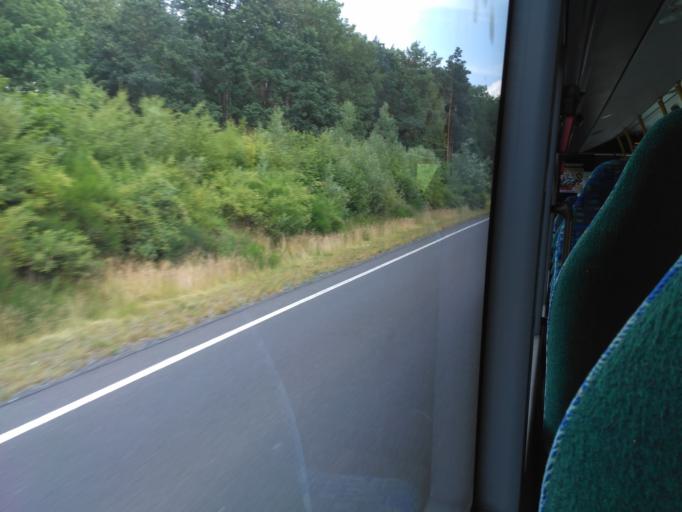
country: DE
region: Saxony
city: Moritzburg
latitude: 51.1590
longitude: 13.6309
